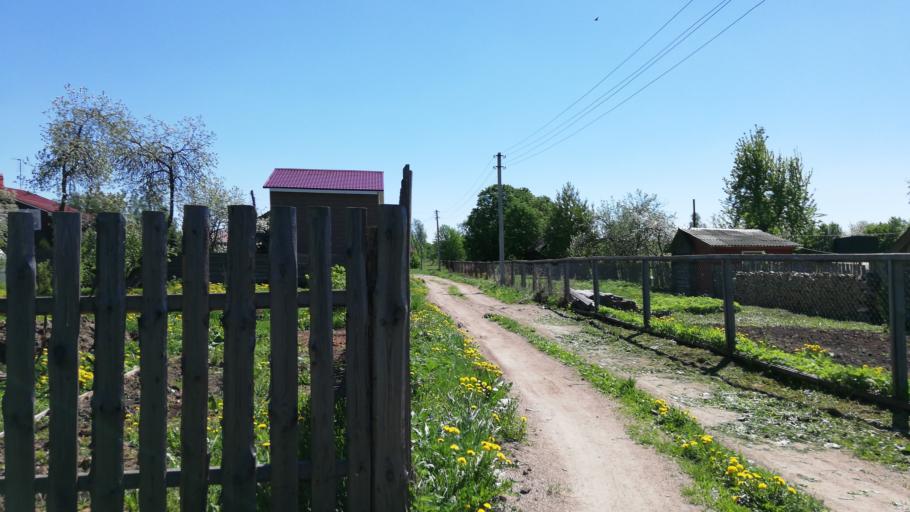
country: RU
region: Ivanovo
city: Pistsovo
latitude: 57.1167
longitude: 40.5955
